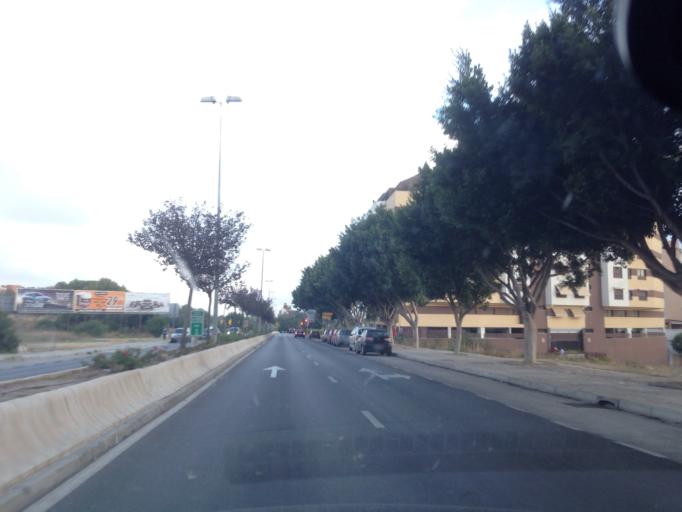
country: ES
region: Andalusia
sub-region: Provincia de Malaga
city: Malaga
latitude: 36.7284
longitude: -4.4650
